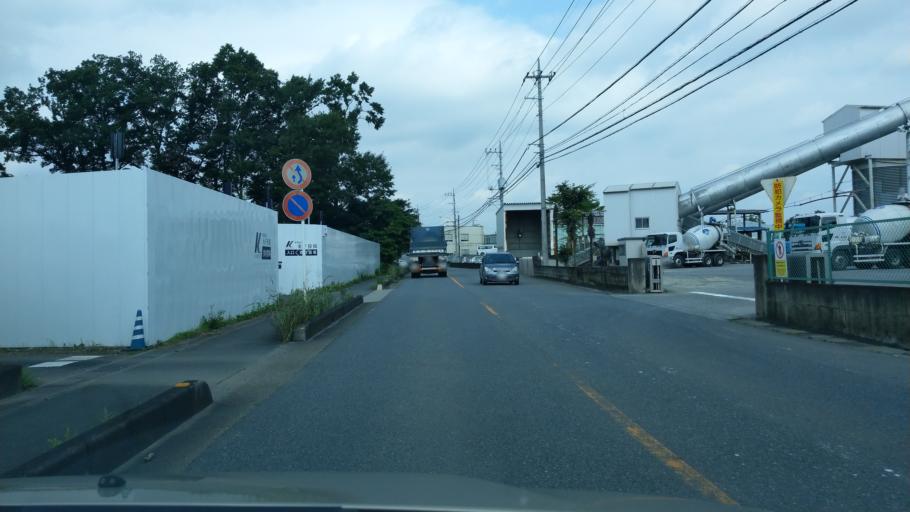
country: JP
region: Saitama
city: Sakado
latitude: 36.0308
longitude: 139.3553
